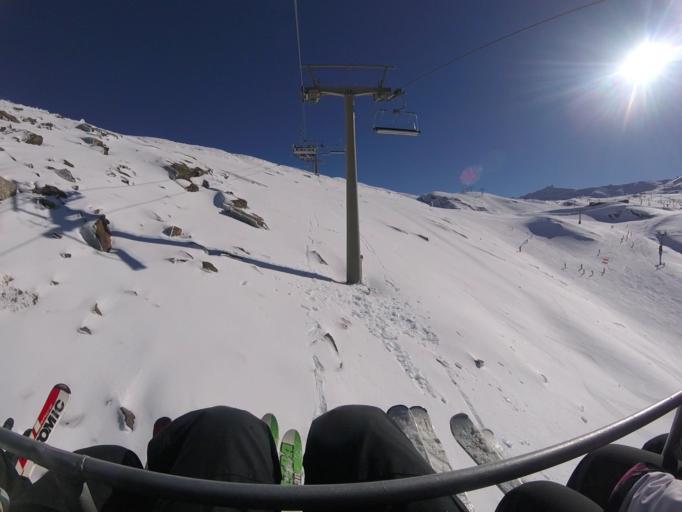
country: ES
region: Andalusia
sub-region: Provincia de Granada
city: Guejar-Sierra
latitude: 37.0745
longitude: -3.3862
